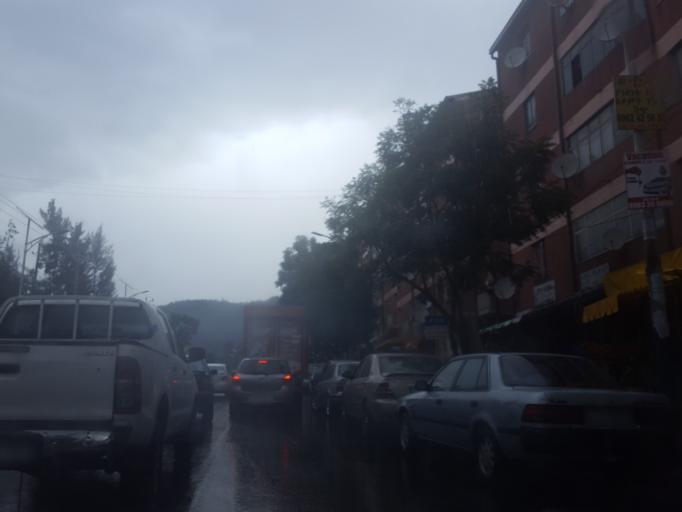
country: ET
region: Adis Abeba
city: Addis Ababa
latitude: 9.0265
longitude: 38.7824
